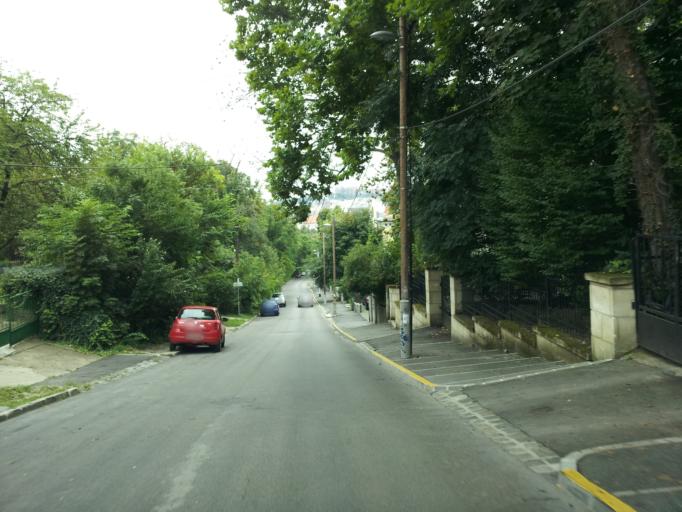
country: HU
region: Budapest
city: Budapest II. keruelet
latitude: 47.5154
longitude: 19.0181
